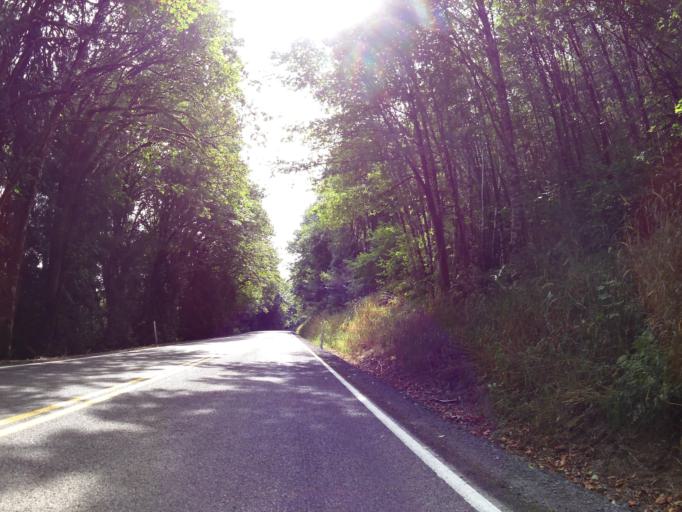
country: US
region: Washington
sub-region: Lewis County
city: Napavine
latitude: 46.5551
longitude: -122.9584
